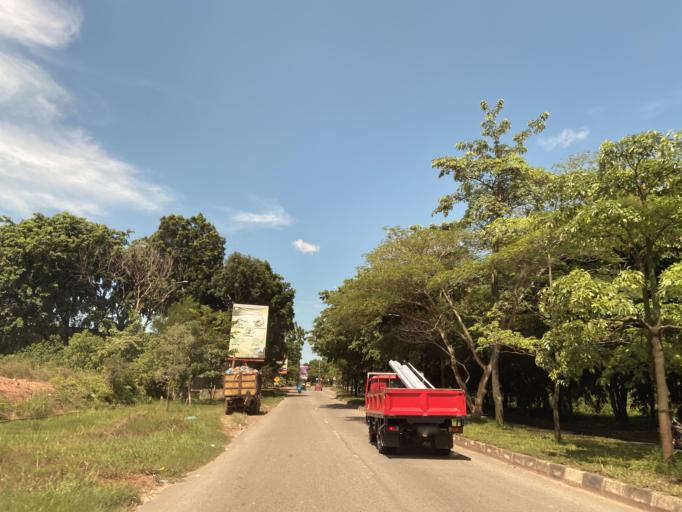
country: SG
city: Singapore
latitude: 1.1087
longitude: 104.0620
